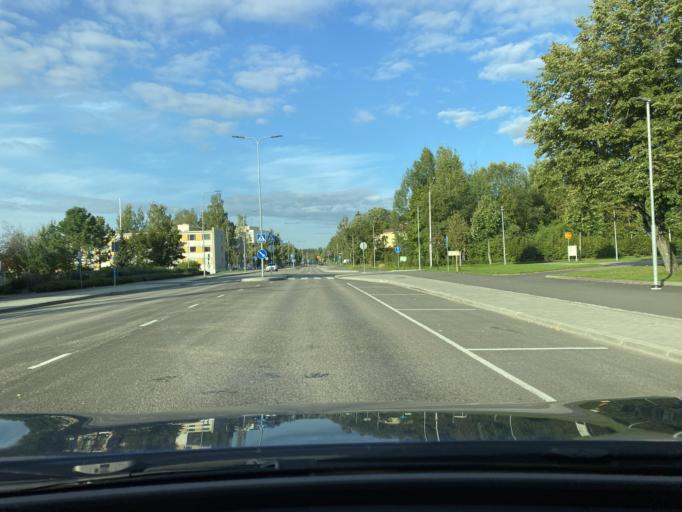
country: FI
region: Kymenlaakso
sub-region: Kouvola
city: Kouvola
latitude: 60.9066
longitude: 26.6199
